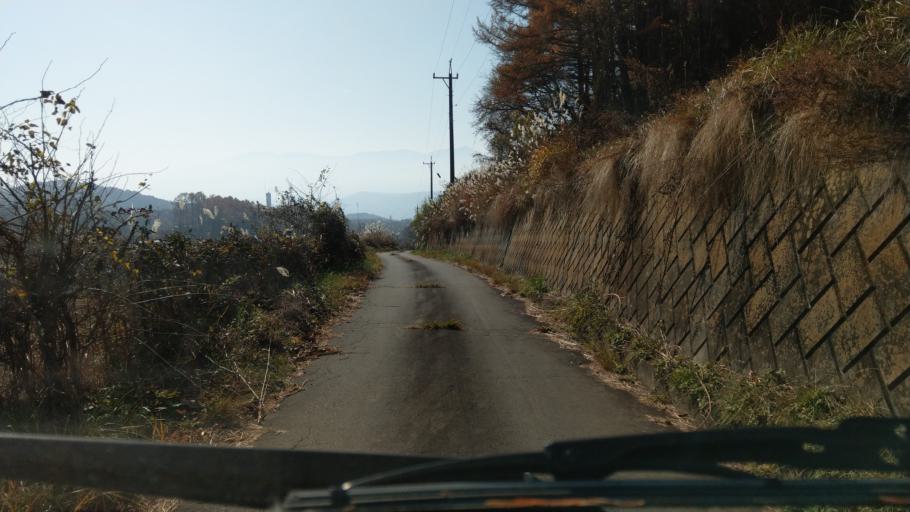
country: JP
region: Nagano
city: Komoro
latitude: 36.3593
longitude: 138.4382
